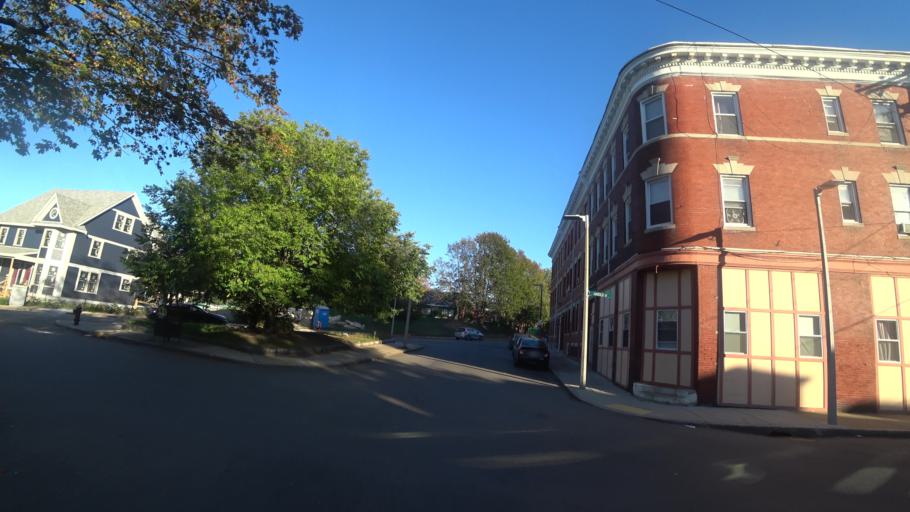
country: US
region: Massachusetts
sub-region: Suffolk County
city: Jamaica Plain
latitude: 42.3143
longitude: -71.0916
